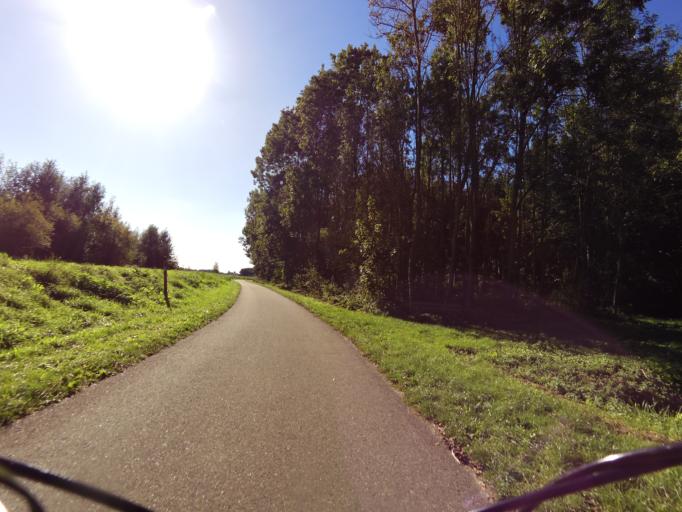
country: NL
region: South Holland
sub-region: Gemeente Voorschoten
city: Voorschoten
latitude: 52.0944
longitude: 4.4260
